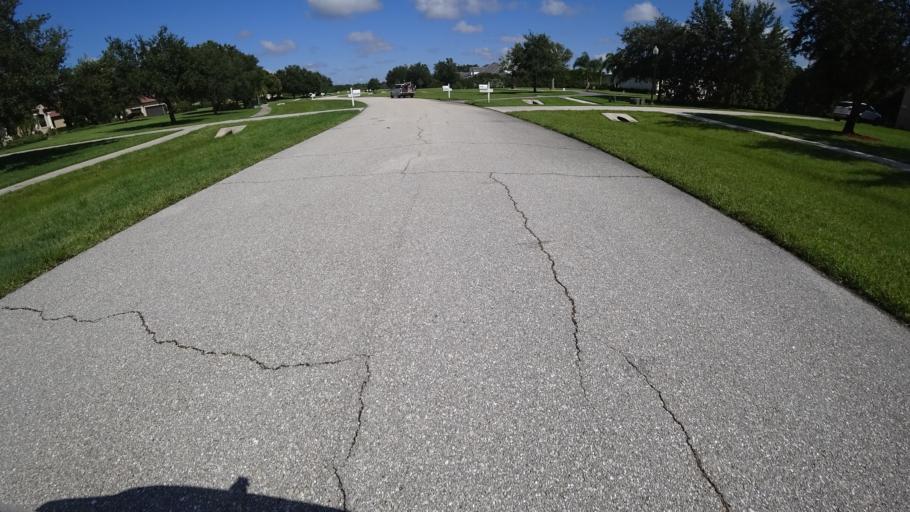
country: US
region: Florida
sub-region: Sarasota County
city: Fruitville
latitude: 27.3907
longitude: -82.3122
